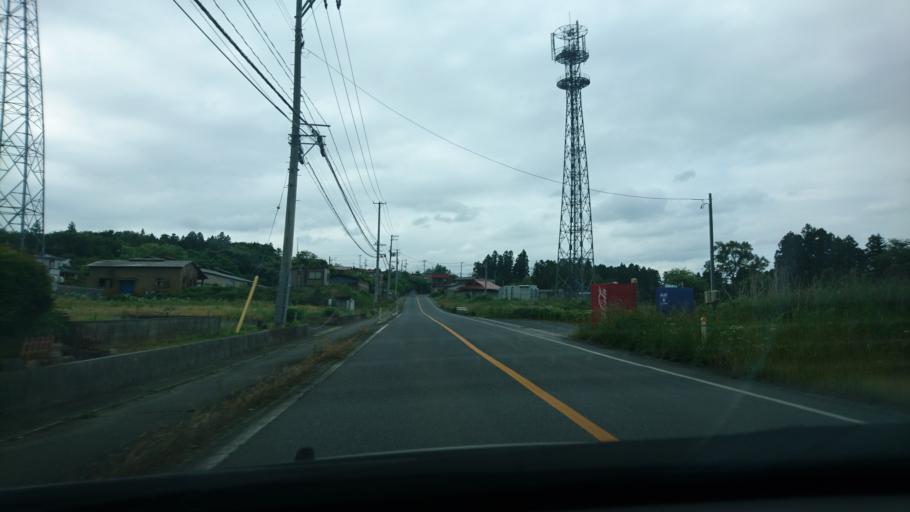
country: JP
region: Iwate
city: Ichinoseki
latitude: 38.8212
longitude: 141.1817
